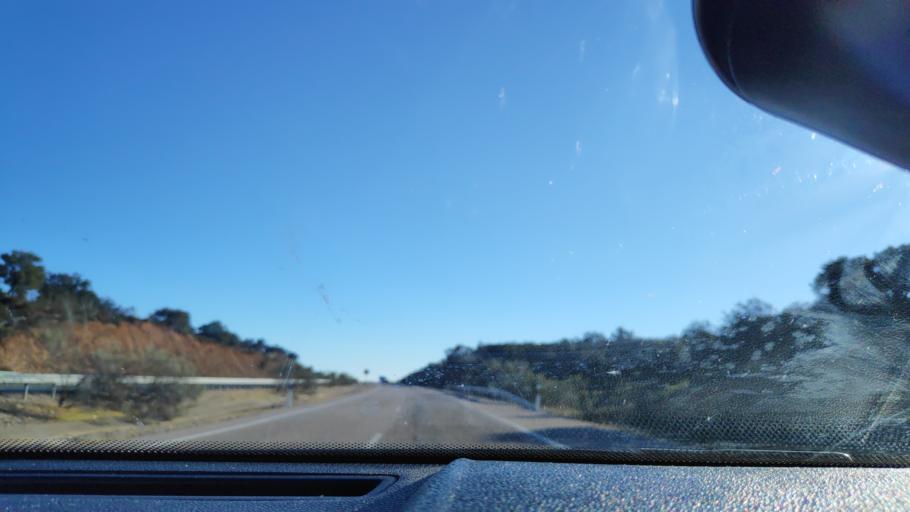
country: ES
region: Andalusia
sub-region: Provincia de Huelva
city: Santa Olalla del Cala
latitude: 37.8753
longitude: -6.2209
